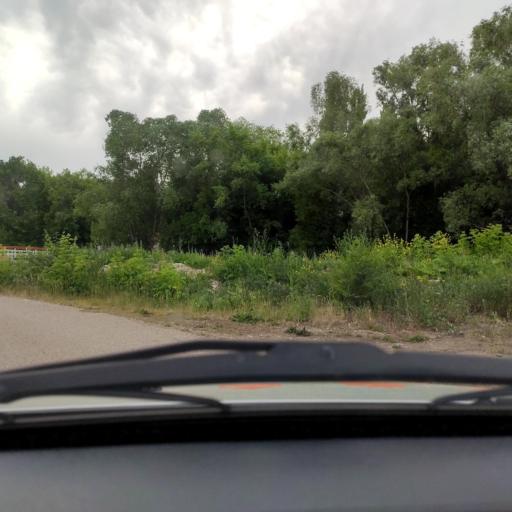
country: RU
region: Bashkortostan
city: Sterlitamak
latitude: 53.6247
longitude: 55.9561
